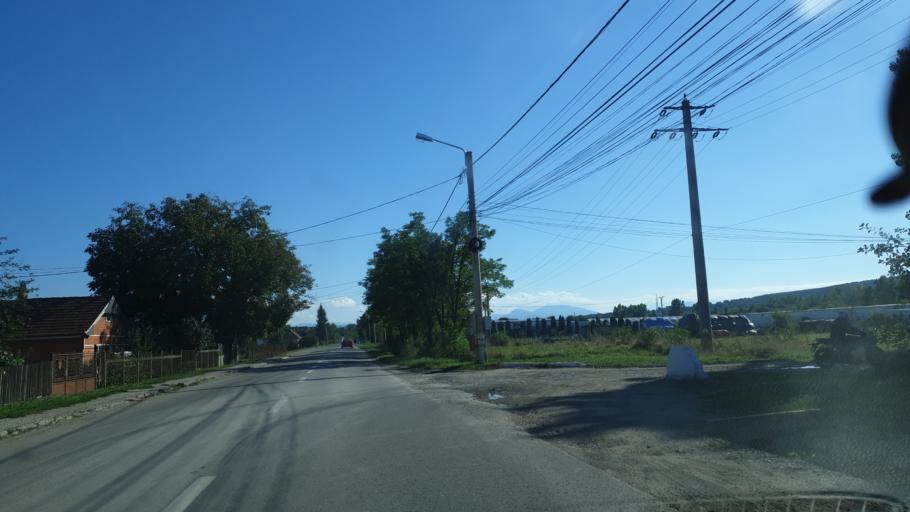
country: RO
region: Covasna
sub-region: Municipiul Sfantu Gheorghe
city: Sfantu-Gheorghe
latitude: 45.8511
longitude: 25.7777
